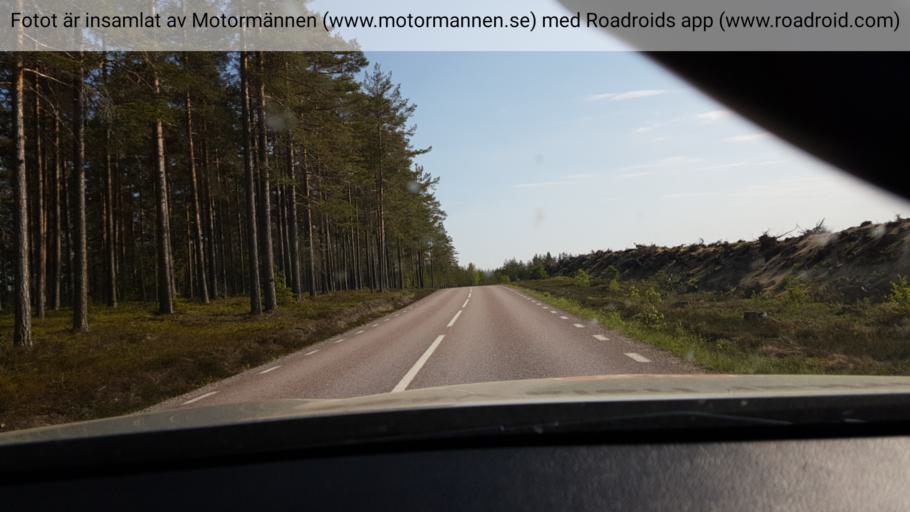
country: SE
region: Gaevleborg
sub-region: Sandvikens Kommun
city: Arsunda
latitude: 60.4735
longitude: 16.7109
